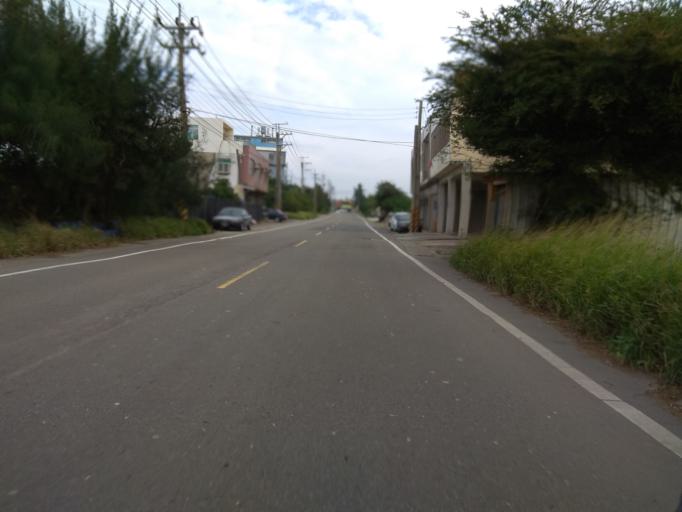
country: TW
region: Taiwan
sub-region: Hsinchu
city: Zhubei
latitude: 24.9850
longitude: 121.0413
